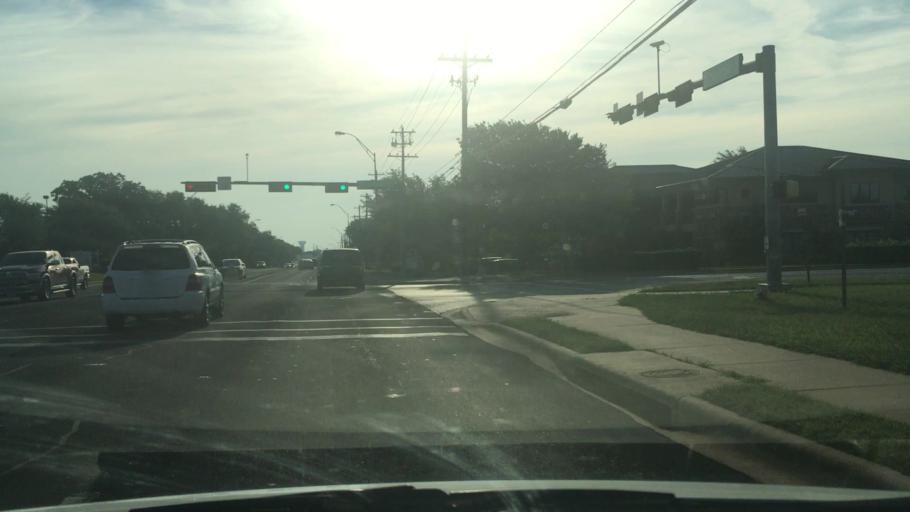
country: US
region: Texas
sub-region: Williamson County
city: Cedar Park
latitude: 30.4749
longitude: -97.8415
